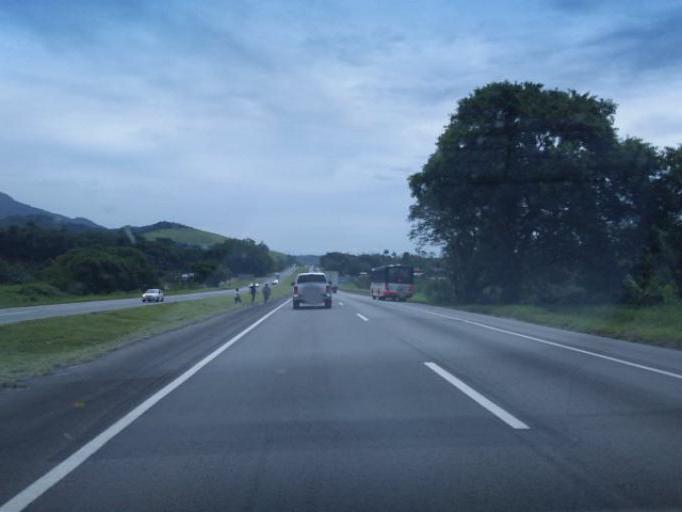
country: BR
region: Sao Paulo
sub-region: Juquia
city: Juquia
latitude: -24.3238
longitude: -47.5505
